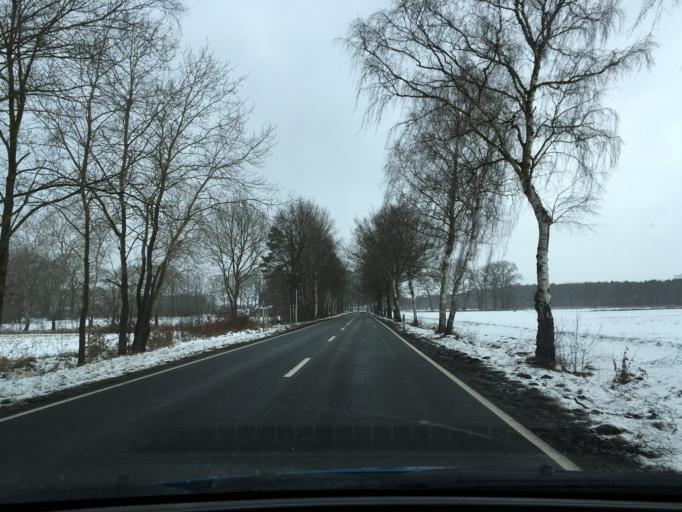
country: DE
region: Lower Saxony
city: Garstedt
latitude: 53.2956
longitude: 10.1923
